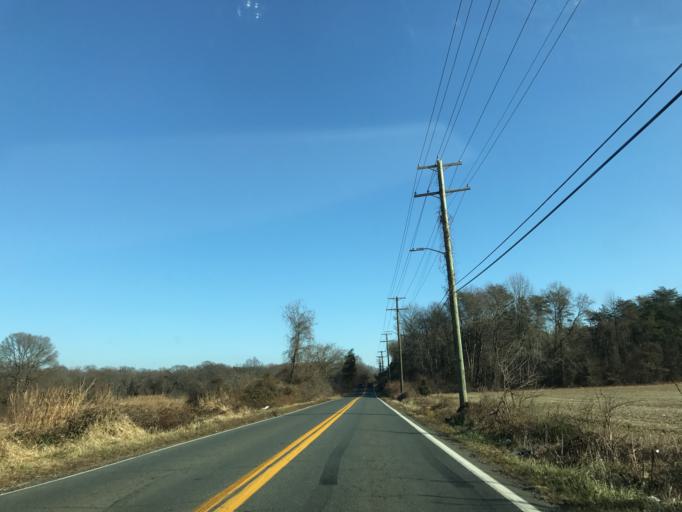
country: US
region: Maryland
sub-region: Baltimore County
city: Bowleys Quarters
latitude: 39.3634
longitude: -76.3976
